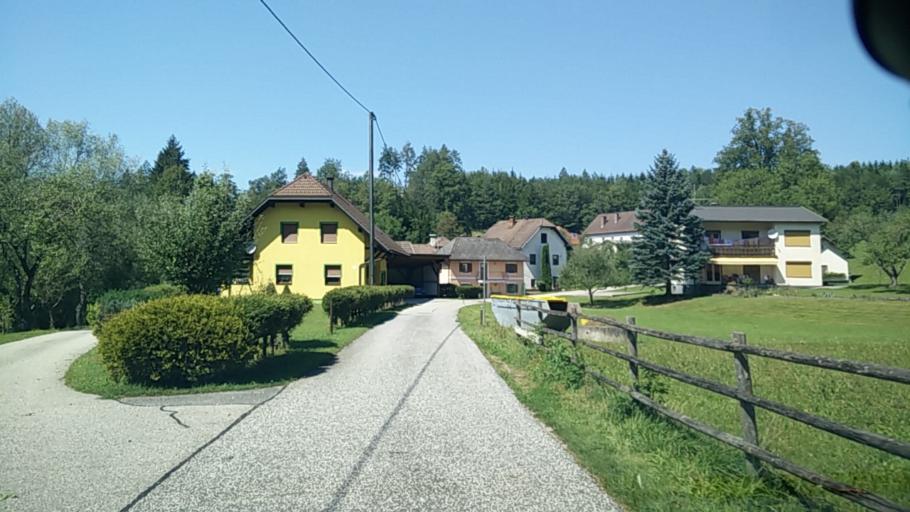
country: AT
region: Carinthia
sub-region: Politischer Bezirk Volkermarkt
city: Sittersdorf
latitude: 46.5384
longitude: 14.5933
